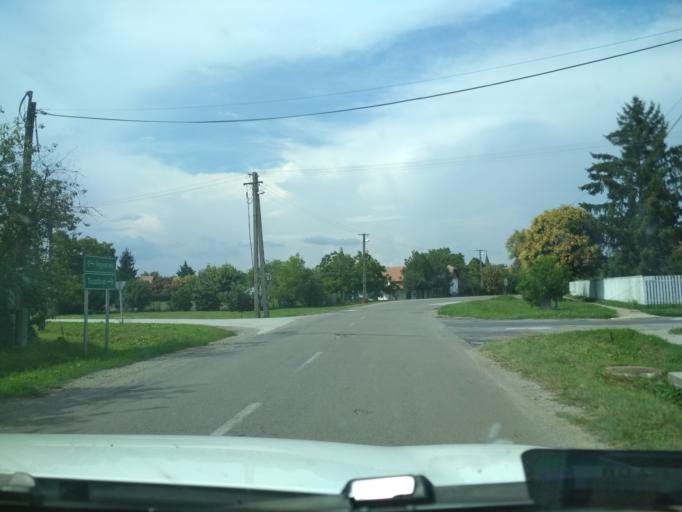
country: HU
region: Jasz-Nagykun-Szolnok
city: Tiszaszolos
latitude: 47.5546
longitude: 20.7195
